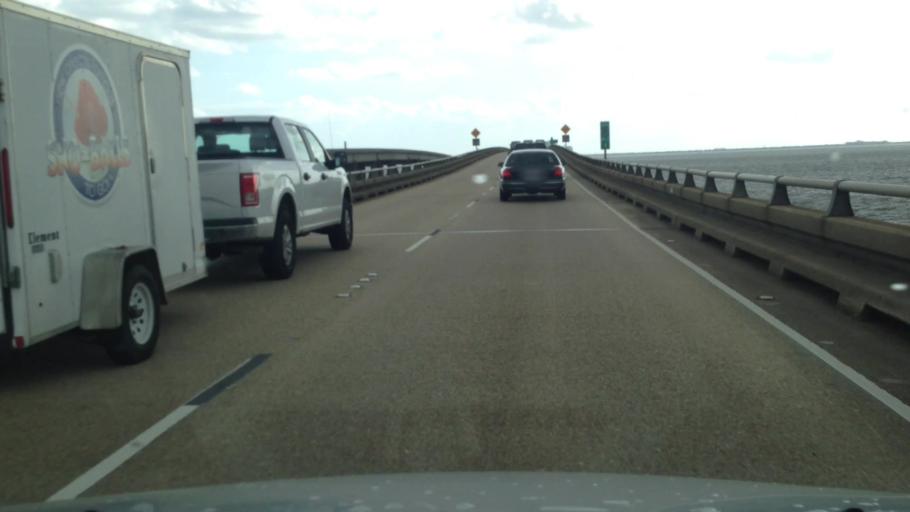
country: US
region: Louisiana
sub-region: Jefferson Parish
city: Metairie
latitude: 30.0796
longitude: -90.1440
